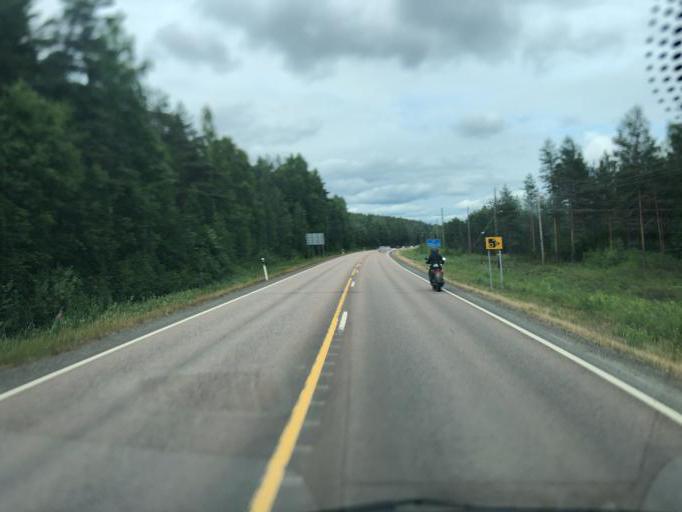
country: FI
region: Kymenlaakso
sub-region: Kouvola
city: Kouvola
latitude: 60.9310
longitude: 26.8030
